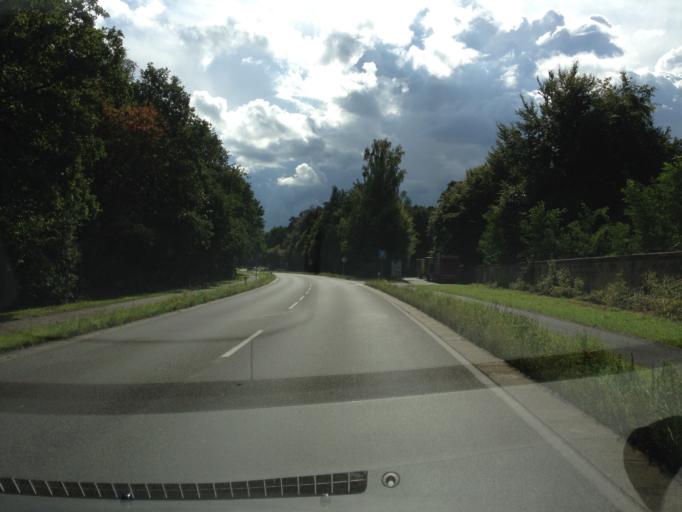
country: DE
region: North Rhine-Westphalia
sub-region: Regierungsbezirk Koln
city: Eil
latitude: 50.9028
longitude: 7.0995
